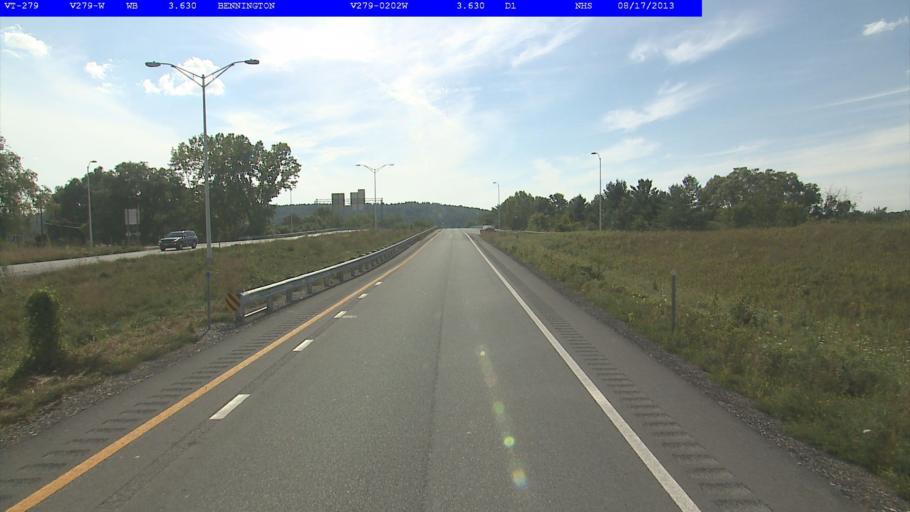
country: US
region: Vermont
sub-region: Bennington County
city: Bennington
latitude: 42.9057
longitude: -73.2093
